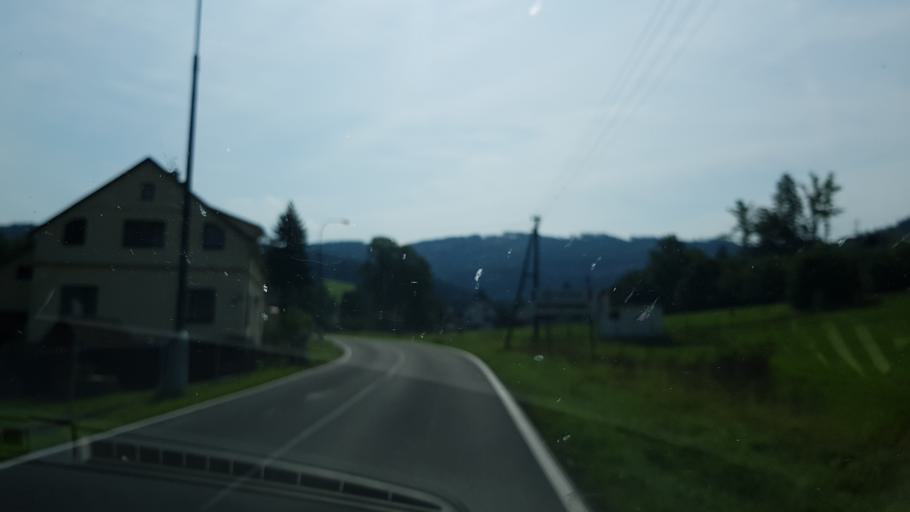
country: CZ
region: Olomoucky
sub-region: Okres Jesenik
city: Jesenik
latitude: 50.2142
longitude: 17.2223
